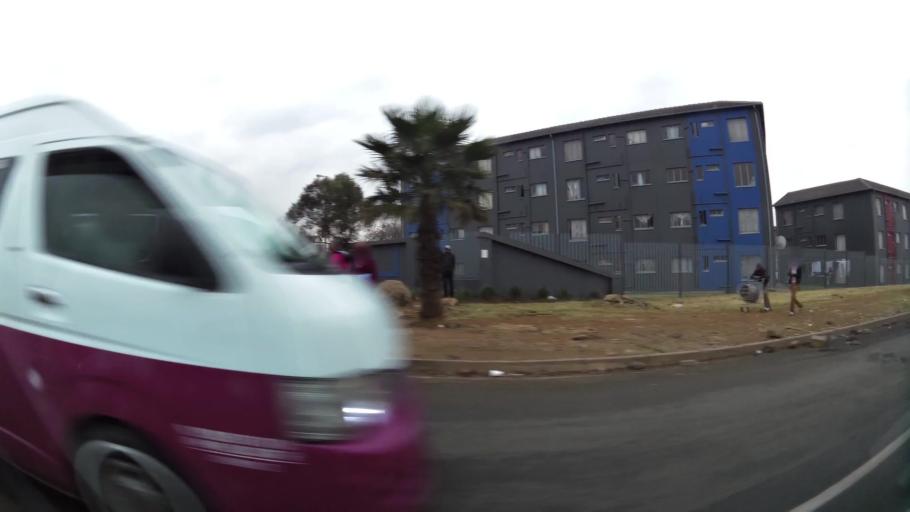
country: ZA
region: Gauteng
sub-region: City of Johannesburg Metropolitan Municipality
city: Soweto
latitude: -26.2454
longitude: 27.8651
